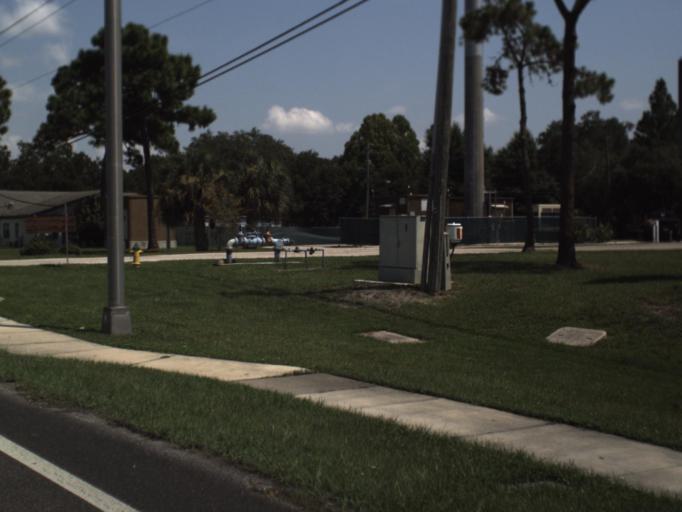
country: US
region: Florida
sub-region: Hillsborough County
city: Carrollwood Village
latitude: 28.0668
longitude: -82.5051
